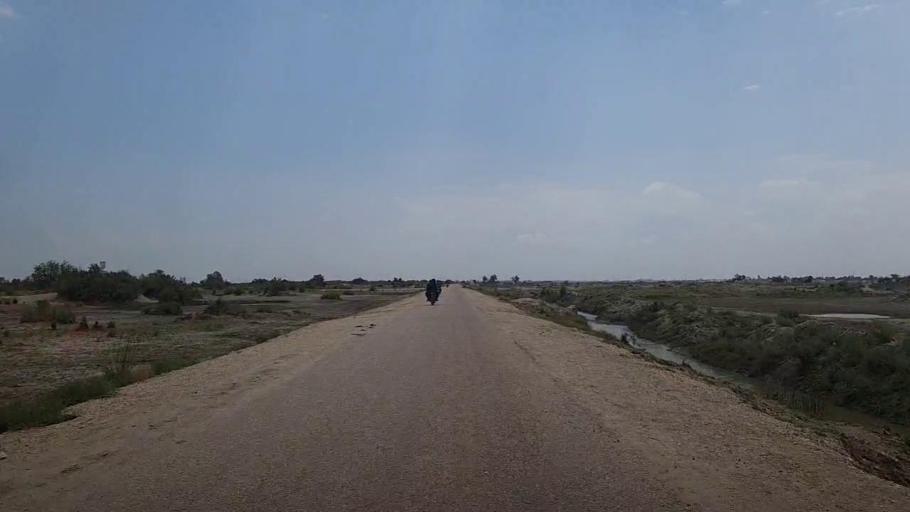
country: PK
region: Sindh
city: Kandhkot
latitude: 28.2916
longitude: 69.1426
